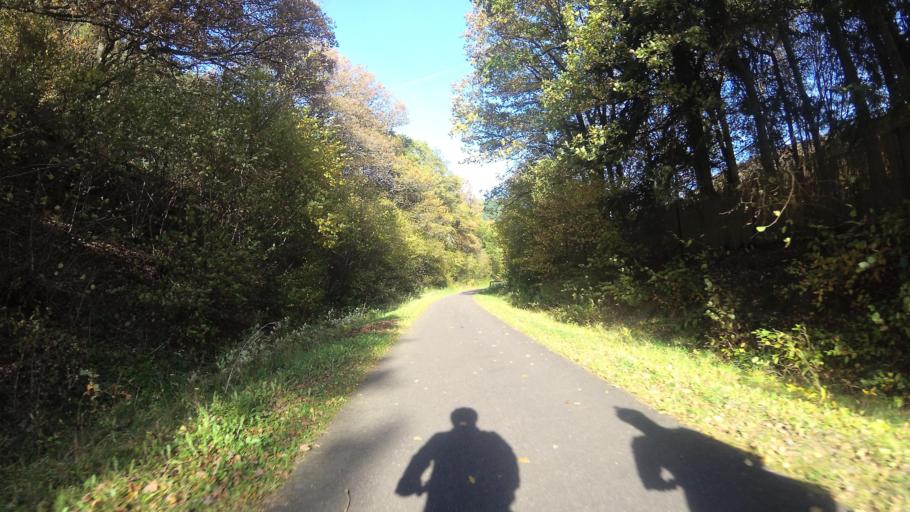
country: DE
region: Rheinland-Pfalz
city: Gusterath
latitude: 49.6986
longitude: 6.7254
